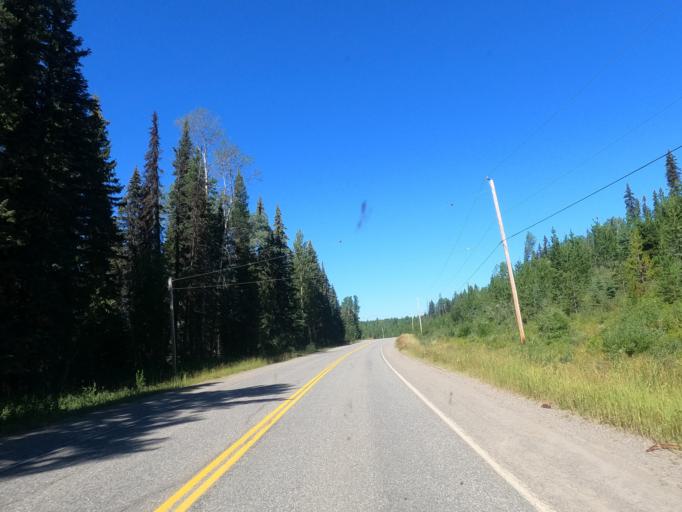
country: CA
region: British Columbia
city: Quesnel
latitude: 53.0283
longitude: -122.0974
